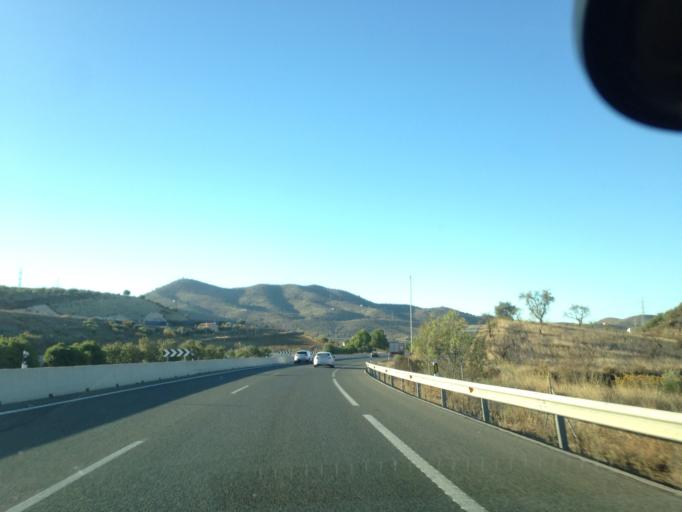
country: ES
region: Andalusia
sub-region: Provincia de Malaga
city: Casabermeja
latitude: 36.9127
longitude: -4.4437
